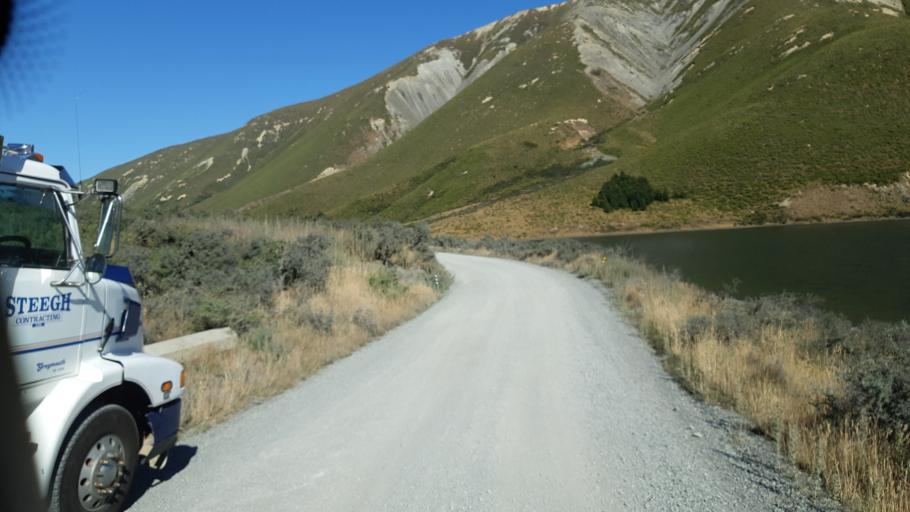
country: NZ
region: Canterbury
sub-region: Ashburton District
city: Methven
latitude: -43.2992
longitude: 171.7086
